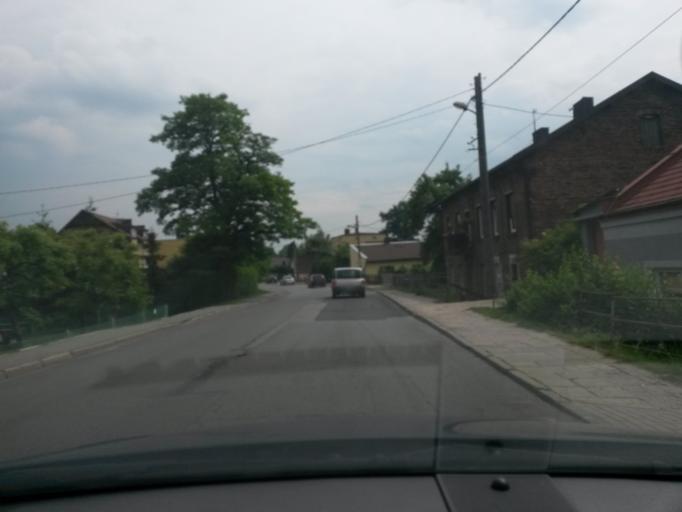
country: PL
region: Silesian Voivodeship
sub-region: Powiat czestochowski
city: Huta Stara B
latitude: 50.7695
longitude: 19.1508
